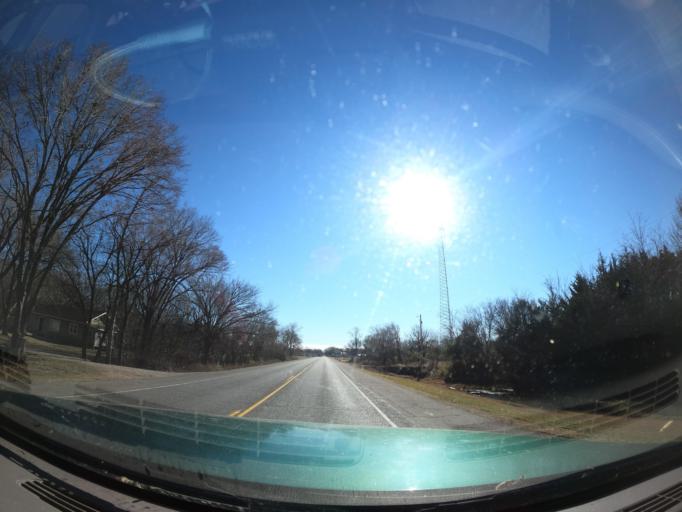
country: US
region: Oklahoma
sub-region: Muskogee County
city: Haskell
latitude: 35.8266
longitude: -95.6775
